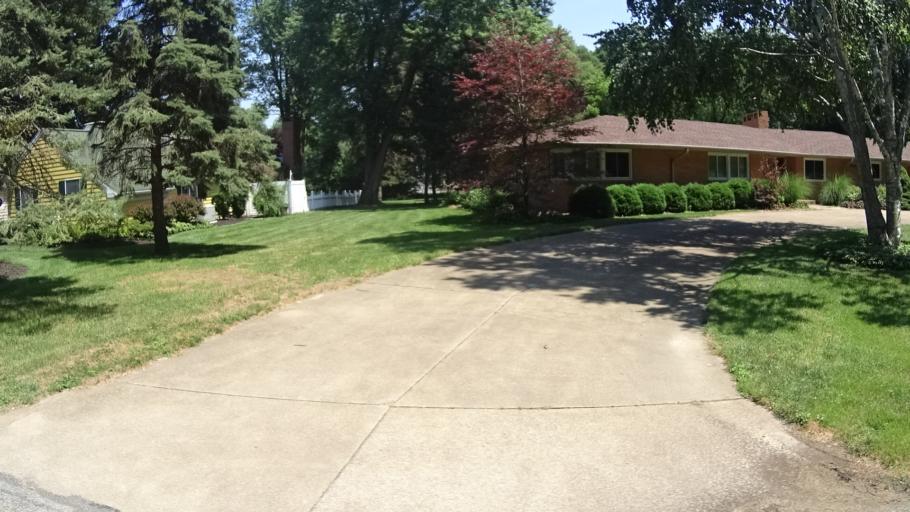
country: US
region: Ohio
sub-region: Erie County
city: Sandusky
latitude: 41.4088
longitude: -82.6449
